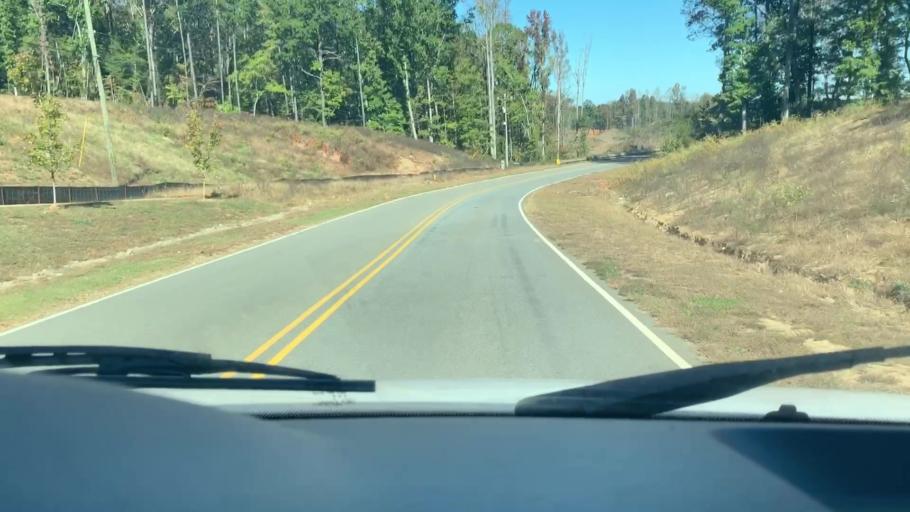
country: US
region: North Carolina
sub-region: Gaston County
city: Davidson
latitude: 35.4626
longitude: -80.8217
